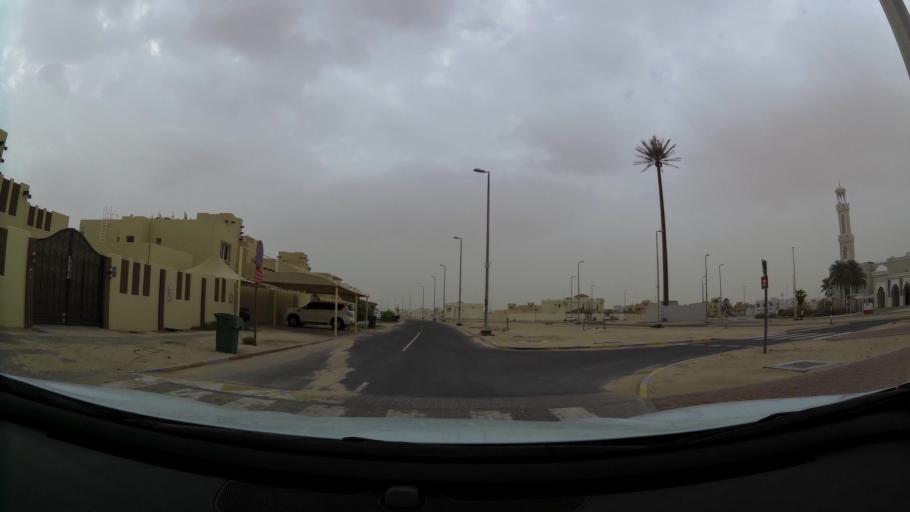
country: AE
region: Abu Dhabi
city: Abu Dhabi
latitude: 24.4463
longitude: 54.7183
